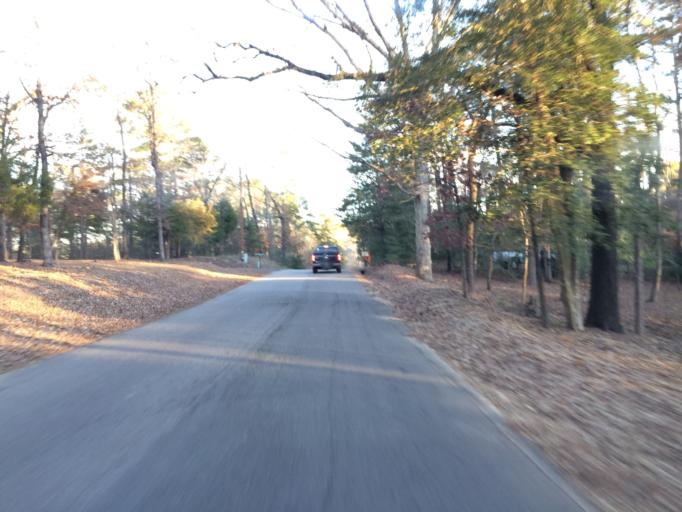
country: US
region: Texas
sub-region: Wood County
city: Hawkins
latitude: 32.7241
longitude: -95.1778
